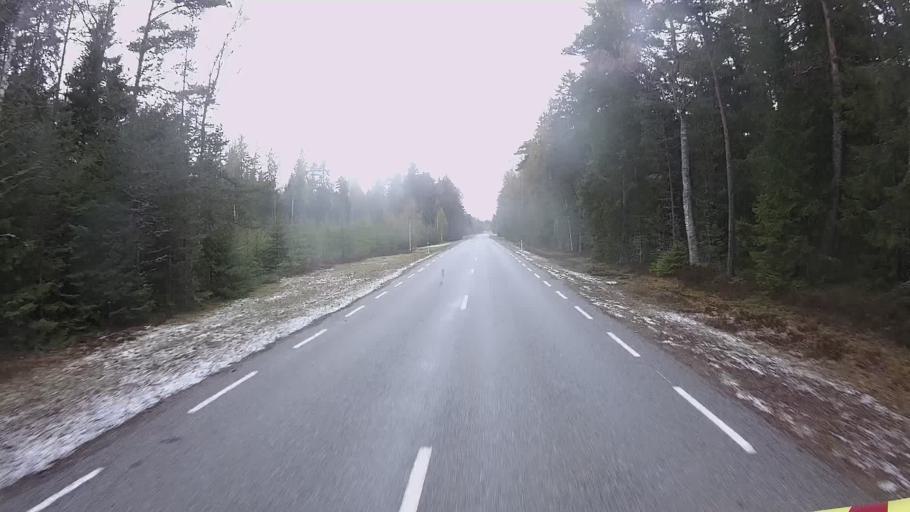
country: EE
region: Hiiumaa
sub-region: Kaerdla linn
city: Kardla
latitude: 59.0634
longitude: 22.6858
